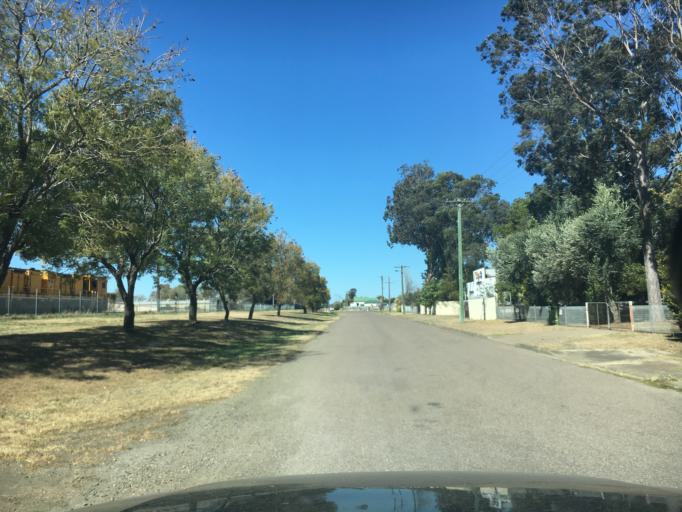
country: AU
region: New South Wales
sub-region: Singleton
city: Singleton
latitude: -32.5734
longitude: 151.1666
